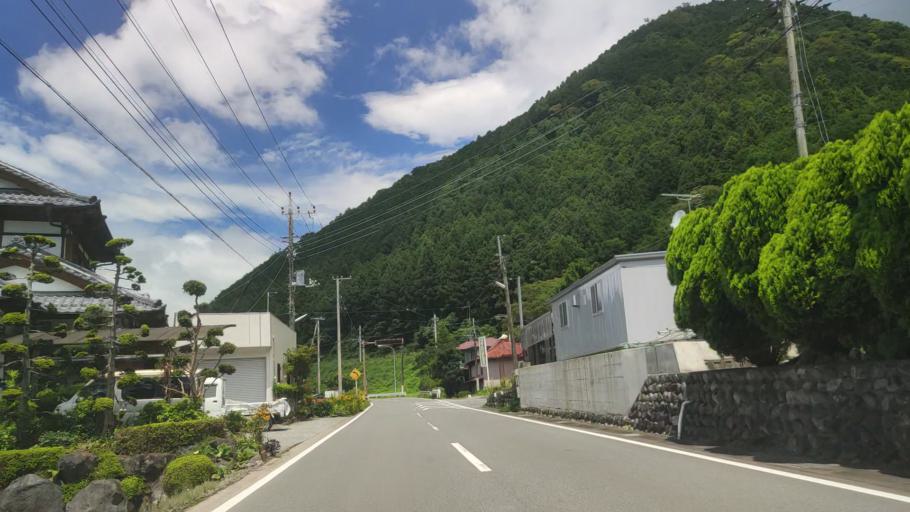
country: JP
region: Shizuoka
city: Fujinomiya
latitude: 35.2926
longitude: 138.4595
